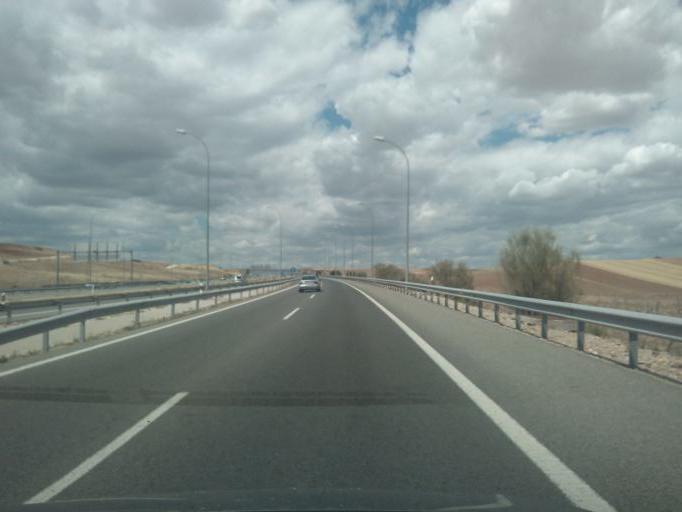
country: ES
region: Madrid
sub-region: Provincia de Madrid
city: Ajalvir
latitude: 40.5196
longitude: -3.5041
